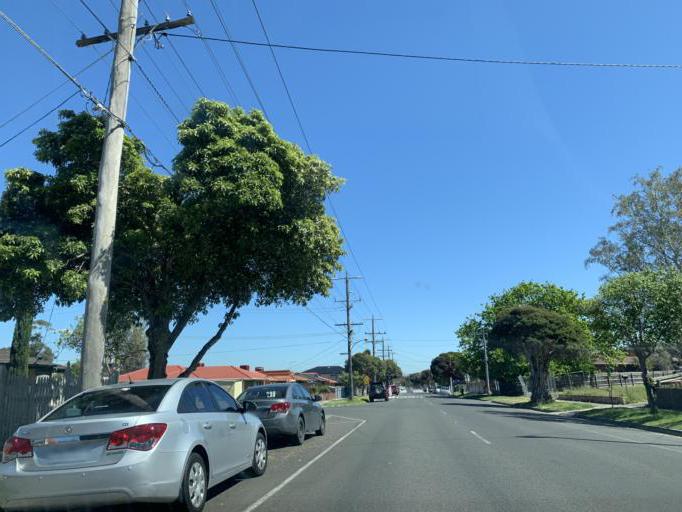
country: AU
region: Victoria
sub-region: Greater Dandenong
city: Dandenong
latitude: -37.9980
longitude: 145.2026
